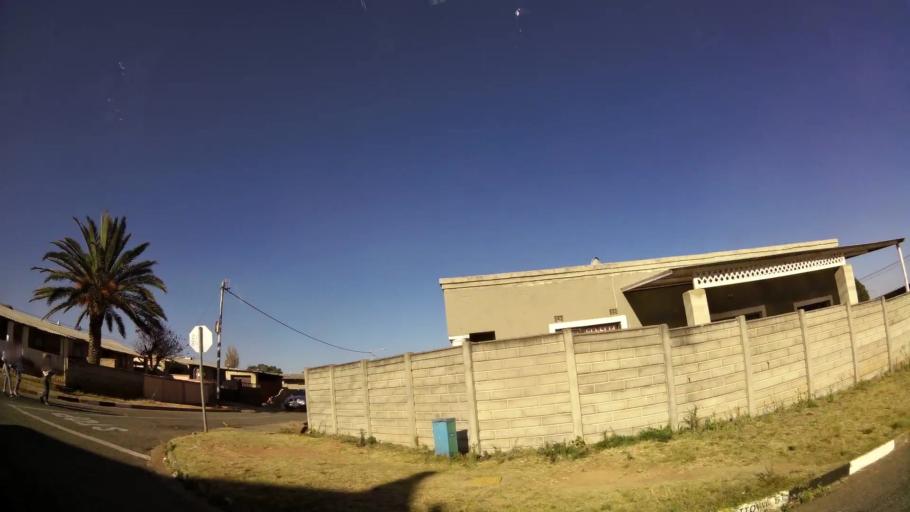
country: ZA
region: Gauteng
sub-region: City of Johannesburg Metropolitan Municipality
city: Johannesburg
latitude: -26.2156
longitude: 27.9802
